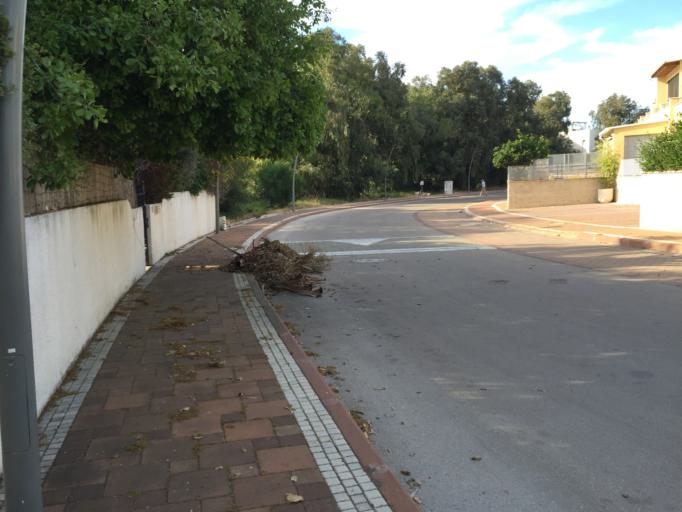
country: IL
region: Haifa
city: Qesarya
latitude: 32.5128
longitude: 34.9016
